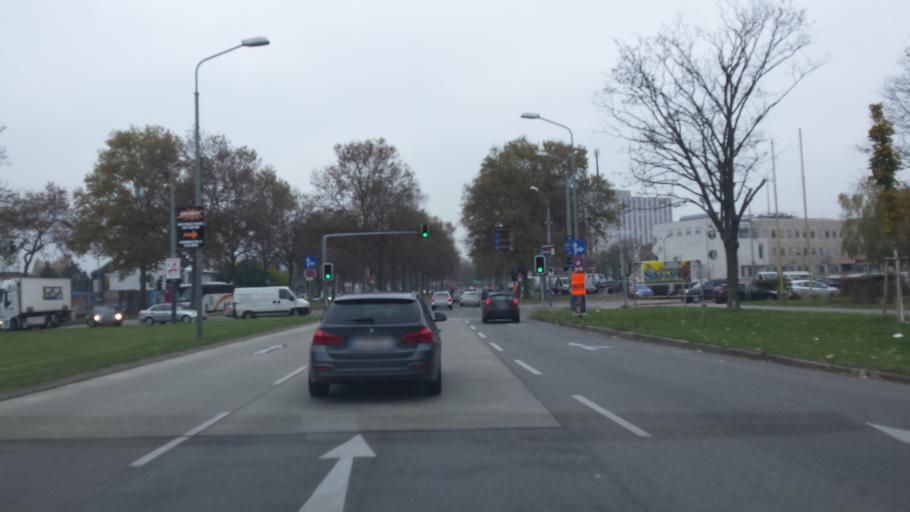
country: AT
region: Lower Austria
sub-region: Politischer Bezirk Wien-Umgebung
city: Gerasdorf bei Wien
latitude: 48.2392
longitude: 16.4383
